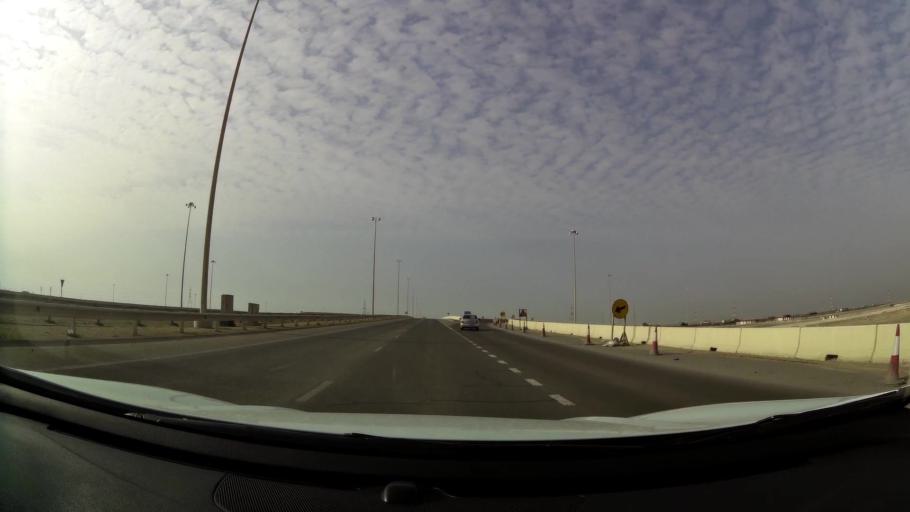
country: AE
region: Abu Dhabi
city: Abu Dhabi
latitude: 24.2106
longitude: 54.4163
